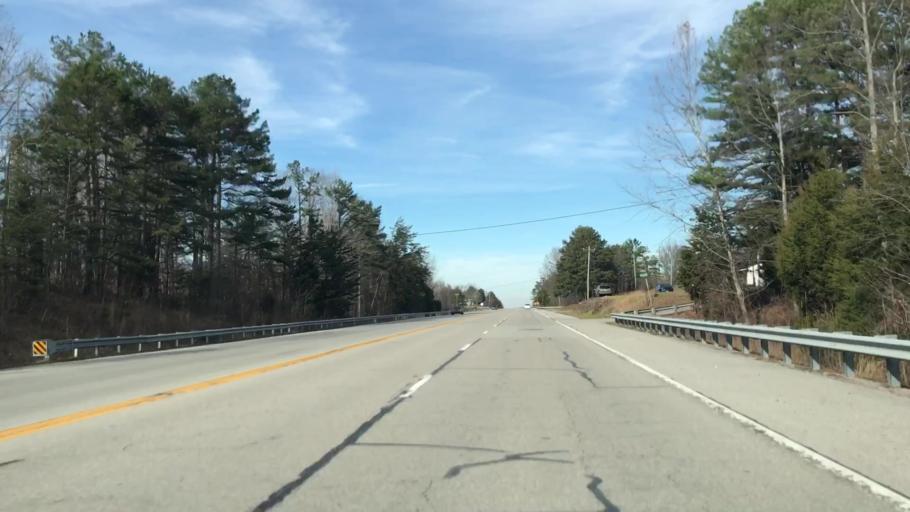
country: US
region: Kentucky
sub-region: Pulaski County
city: Somerset
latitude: 36.9208
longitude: -84.5183
